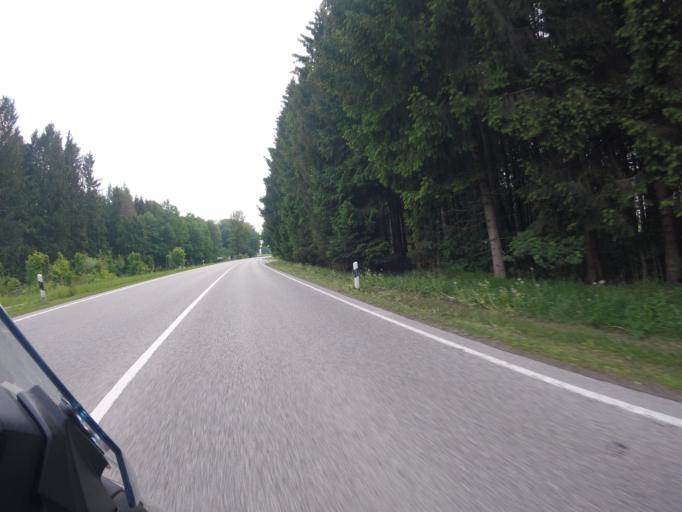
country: DE
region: Bavaria
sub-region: Upper Bavaria
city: Icking
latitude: 47.9347
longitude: 11.4230
